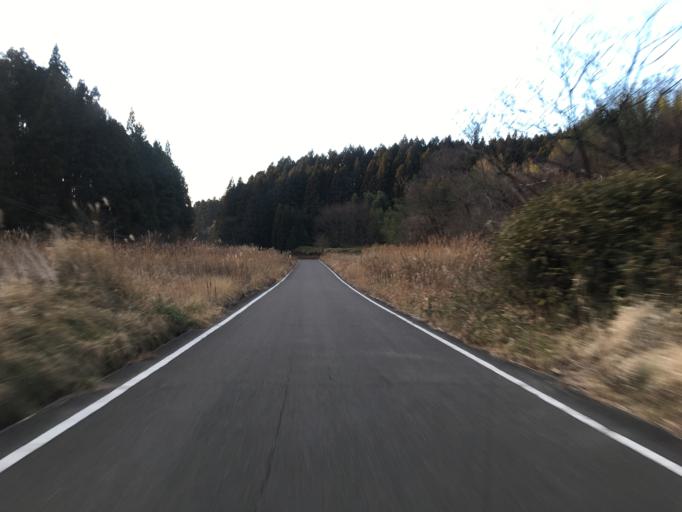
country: JP
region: Fukushima
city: Ishikawa
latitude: 37.1905
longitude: 140.5888
